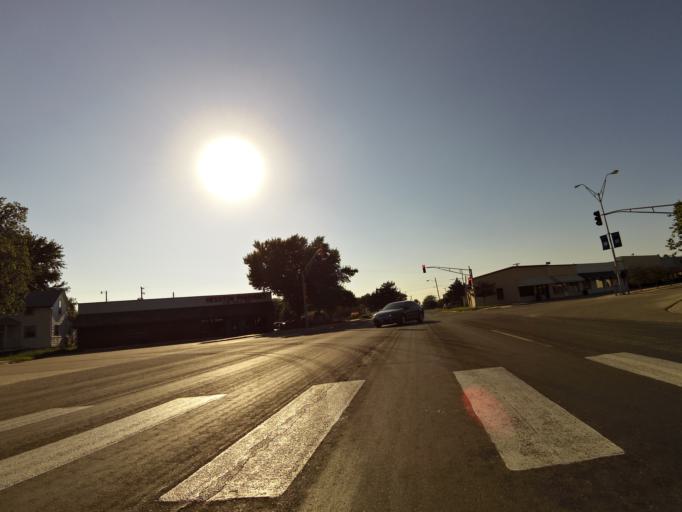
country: US
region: Kansas
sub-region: Harvey County
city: Hesston
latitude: 38.1383
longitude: -97.4314
